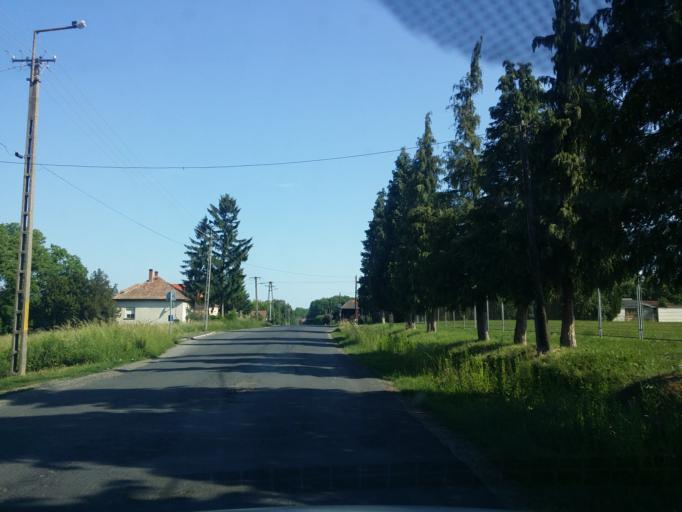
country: HU
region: Zala
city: Zalaszentgrot
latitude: 46.8673
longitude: 17.1157
